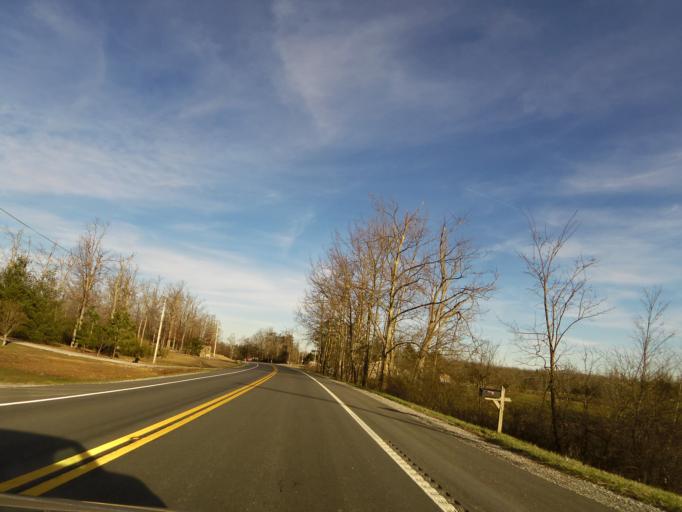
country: US
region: Tennessee
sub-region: Putnam County
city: Monterey
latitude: 35.9642
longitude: -85.2440
